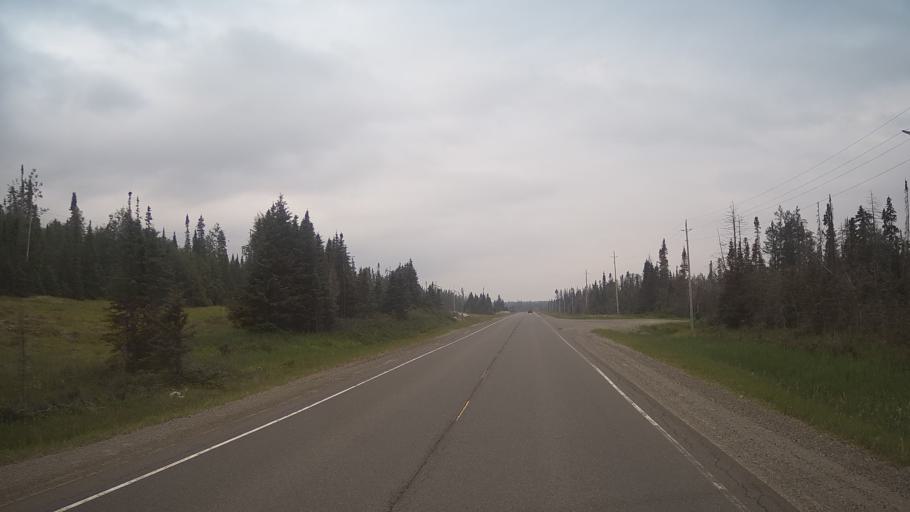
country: CA
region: Ontario
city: Greenstone
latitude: 49.5500
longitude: -87.9933
